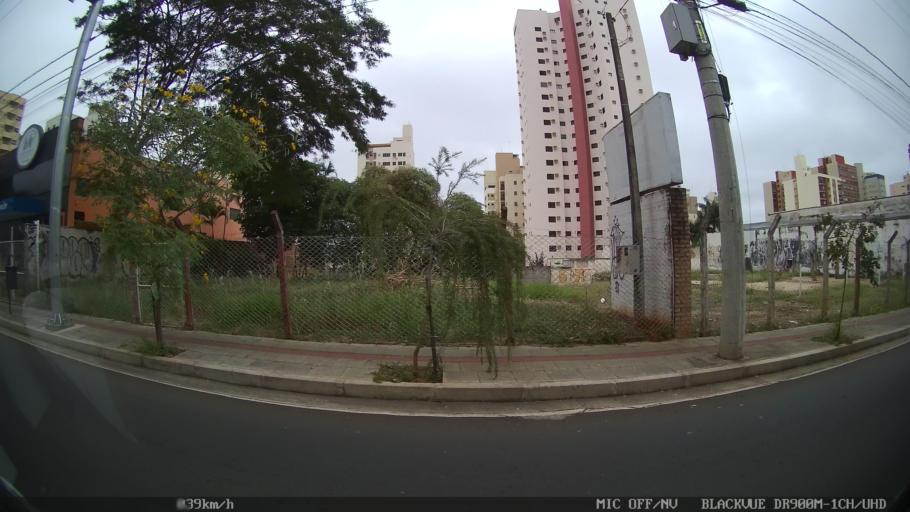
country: BR
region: Sao Paulo
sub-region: Sao Jose Do Rio Preto
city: Sao Jose do Rio Preto
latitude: -20.8160
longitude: -49.3869
